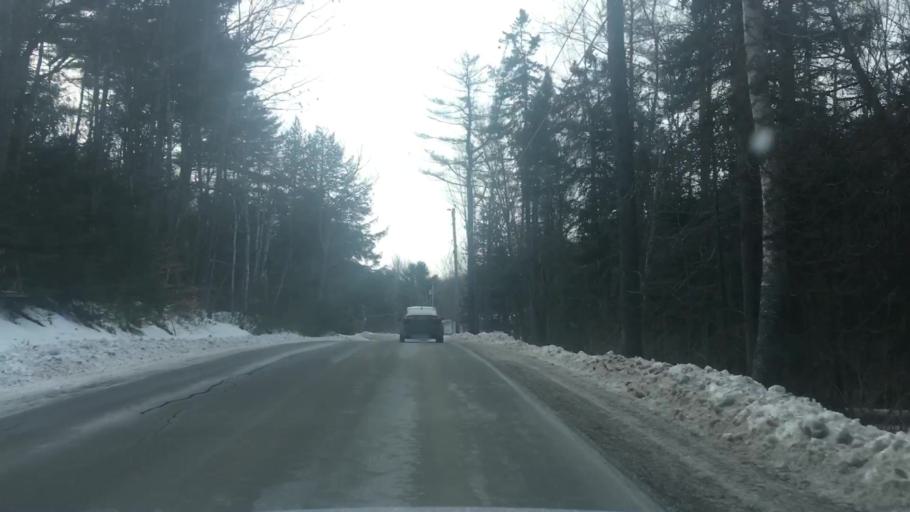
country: US
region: Maine
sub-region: Hancock County
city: Orland
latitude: 44.6165
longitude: -68.7087
